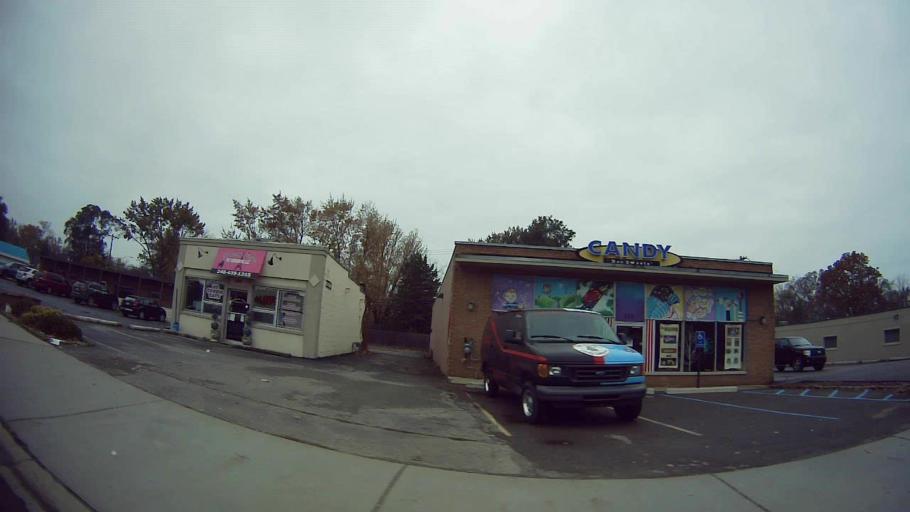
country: US
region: Michigan
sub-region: Oakland County
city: Clawson
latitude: 42.5349
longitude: -83.1356
